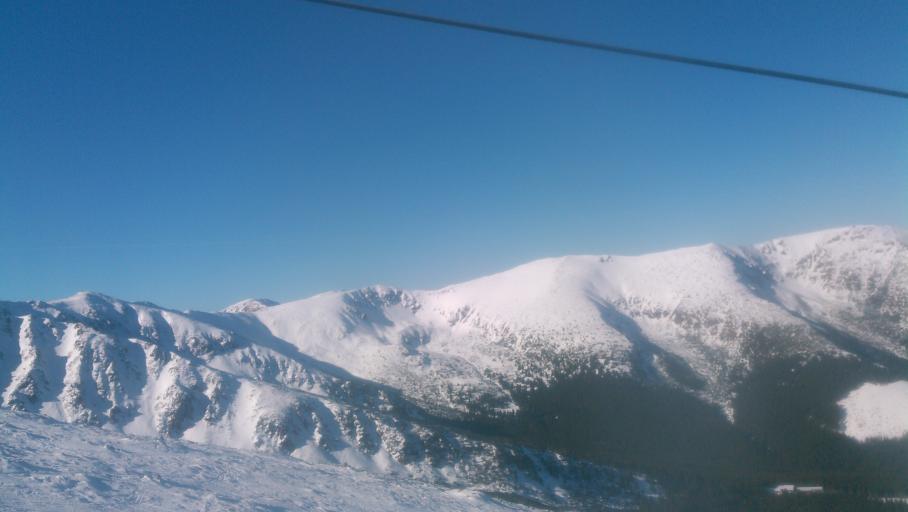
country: SK
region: Zilinsky
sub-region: Okres Liptovsky Mikulas
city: Liptovsky Mikulas
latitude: 48.9500
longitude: 19.5900
